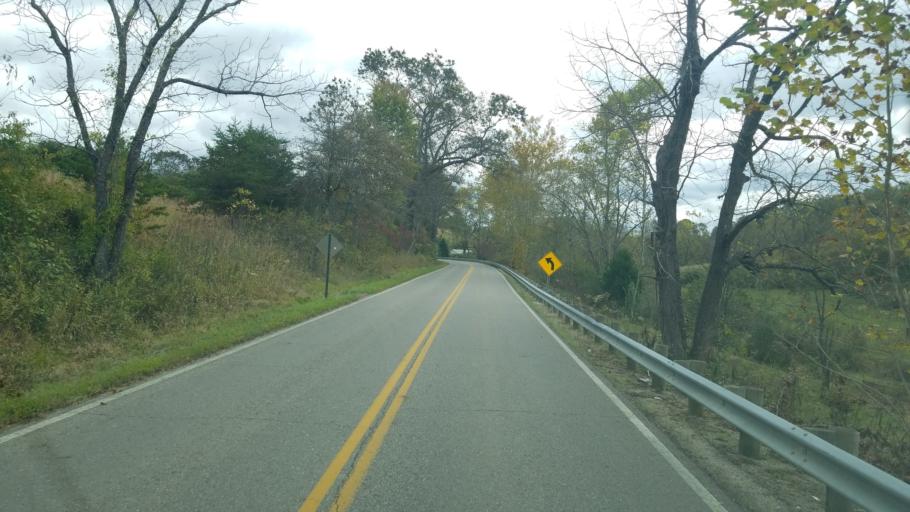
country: US
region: Ohio
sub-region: Jackson County
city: Jackson
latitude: 39.1257
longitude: -82.6361
